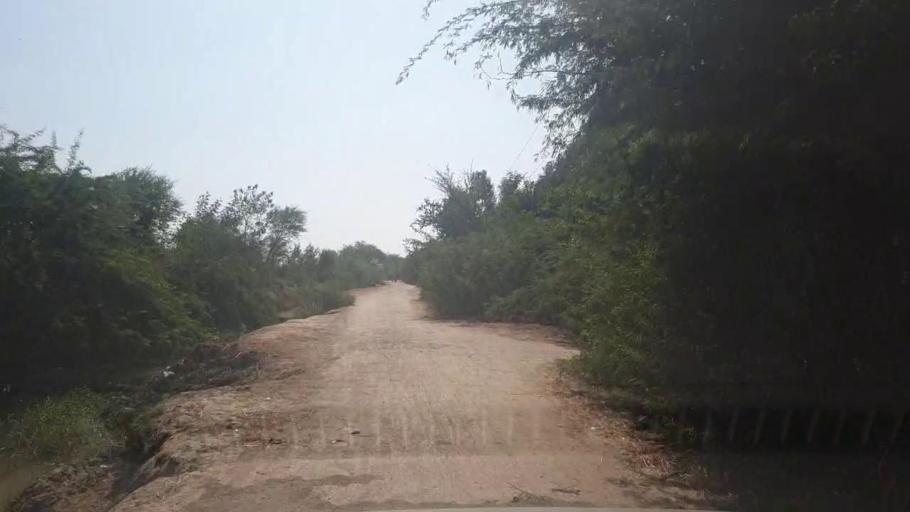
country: PK
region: Sindh
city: Badin
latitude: 24.6824
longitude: 68.8787
